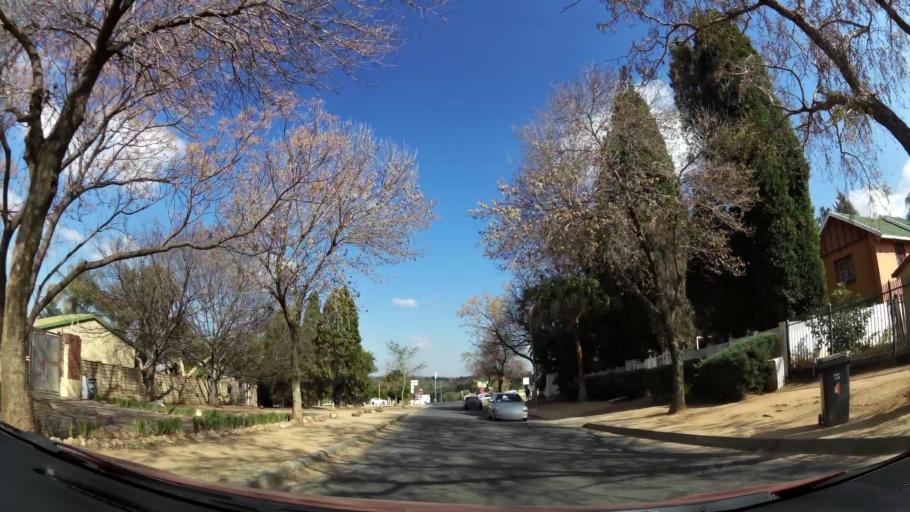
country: ZA
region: Gauteng
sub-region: West Rand District Municipality
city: Muldersdriseloop
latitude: -26.0644
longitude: 27.9601
